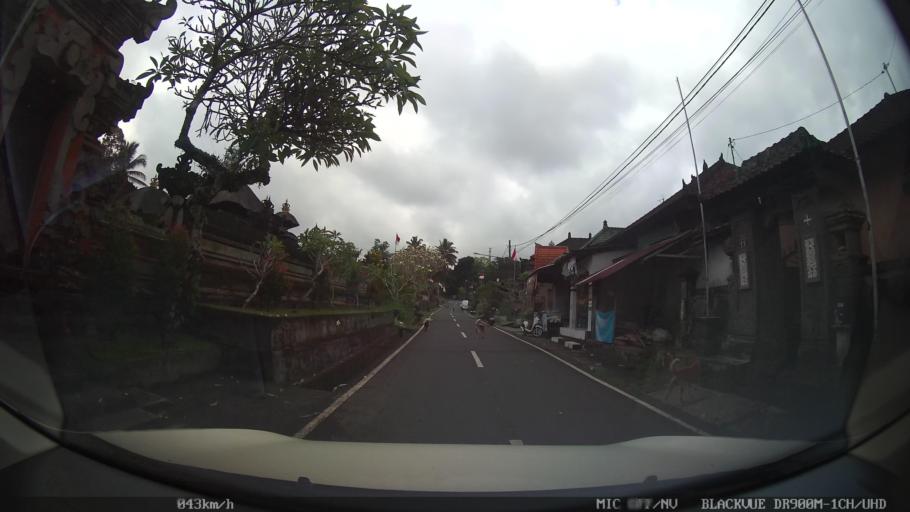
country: ID
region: Bali
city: Pemijian
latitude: -8.4442
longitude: 115.2265
